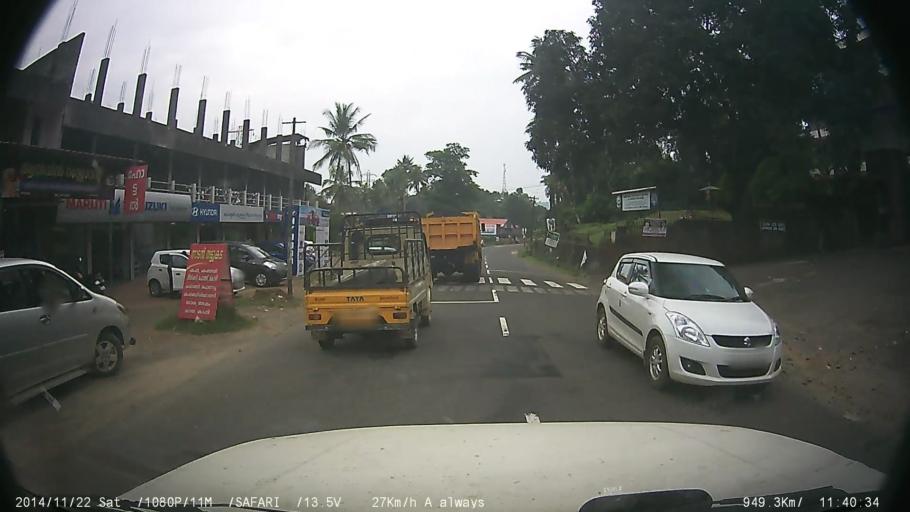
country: IN
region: Kerala
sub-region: Ernakulam
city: Piravam
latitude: 9.8694
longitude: 76.5965
